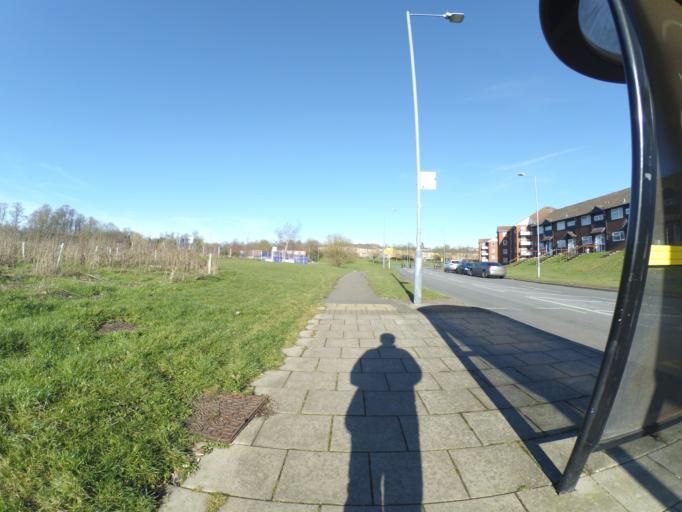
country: GB
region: England
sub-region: Warwickshire
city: Rugby
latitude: 52.3902
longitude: -1.2507
